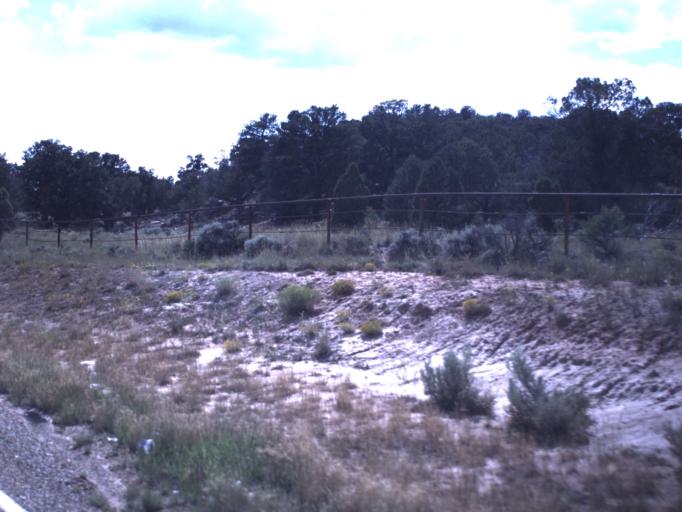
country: US
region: Utah
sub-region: Duchesne County
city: Duchesne
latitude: 40.2842
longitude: -110.7000
